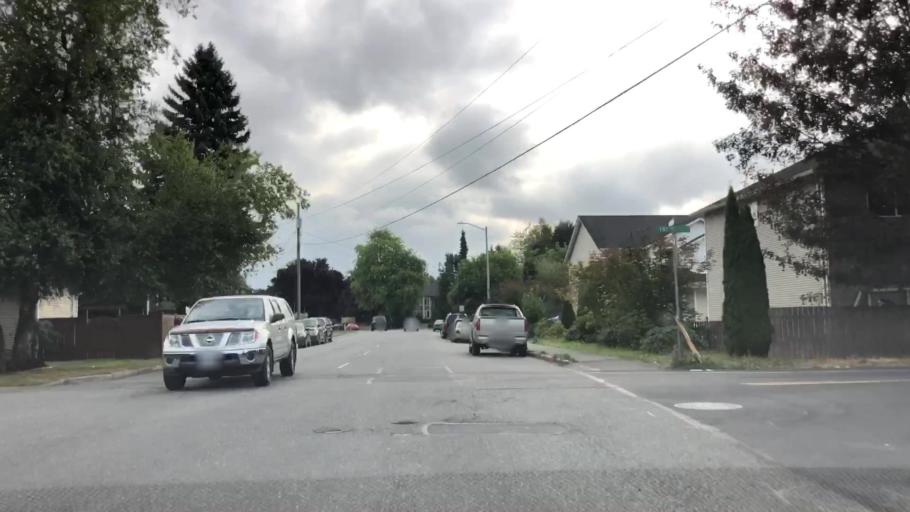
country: US
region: Washington
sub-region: Snohomish County
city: Monroe
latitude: 47.8577
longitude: -121.9869
